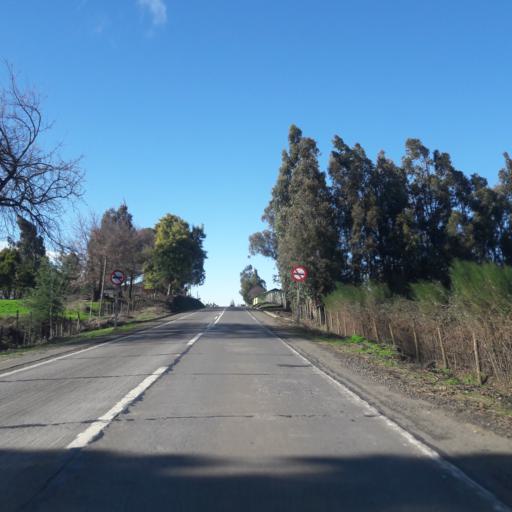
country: CL
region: Araucania
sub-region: Provincia de Malleco
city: Angol
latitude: -37.7658
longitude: -72.5608
